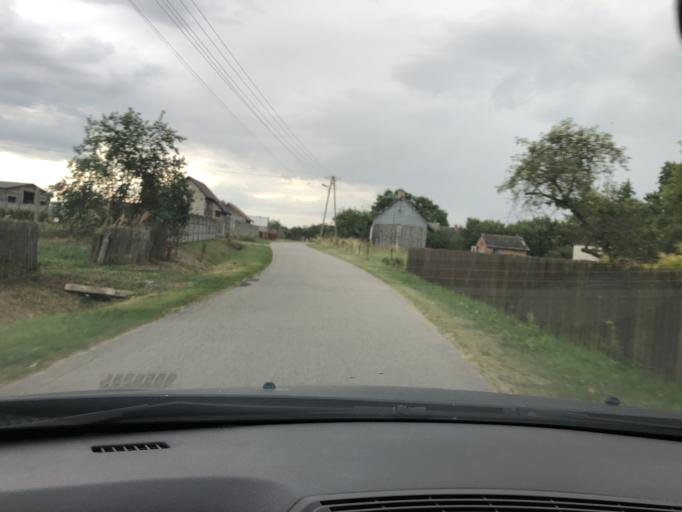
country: PL
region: Lodz Voivodeship
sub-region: Powiat wieruszowski
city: Czastary
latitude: 51.2417
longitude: 18.2820
